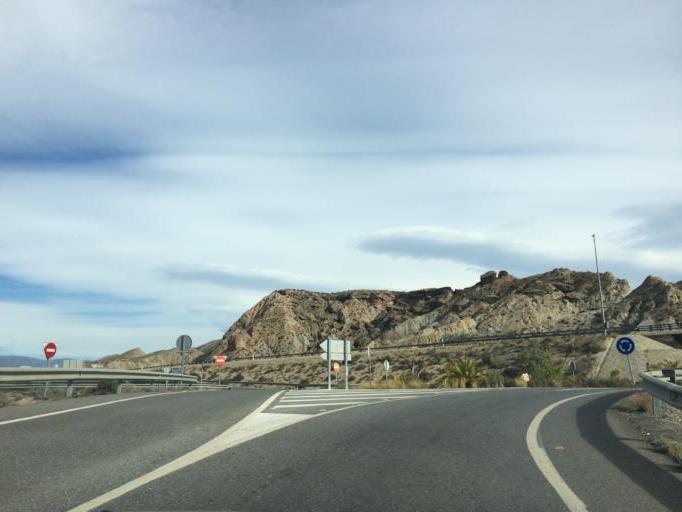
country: ES
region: Andalusia
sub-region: Provincia de Almeria
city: Rioja
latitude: 36.9610
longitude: -2.4671
